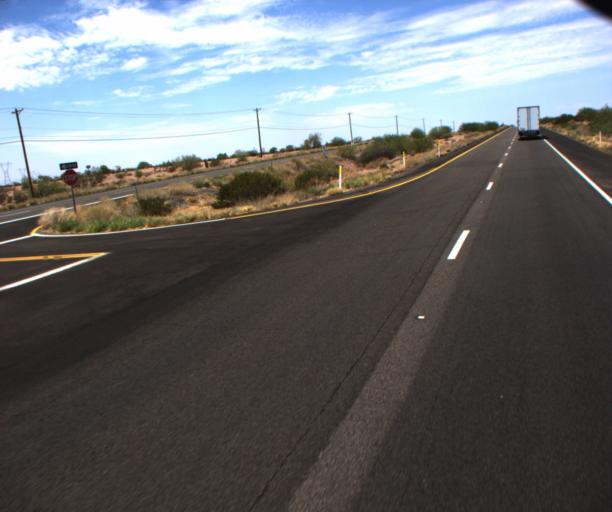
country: US
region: Arizona
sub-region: Pinal County
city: Gold Camp
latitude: 33.2784
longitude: -111.3662
